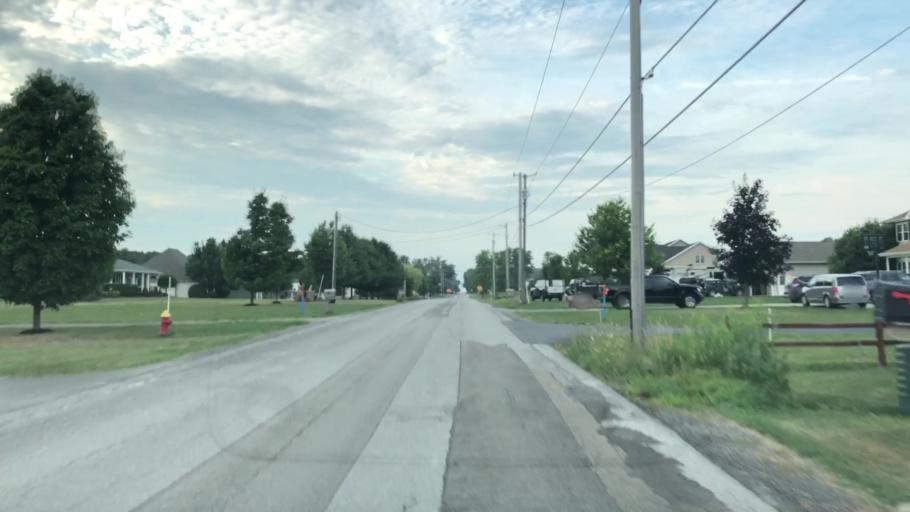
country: US
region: New York
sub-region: Erie County
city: Billington Heights
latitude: 42.8015
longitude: -78.6059
